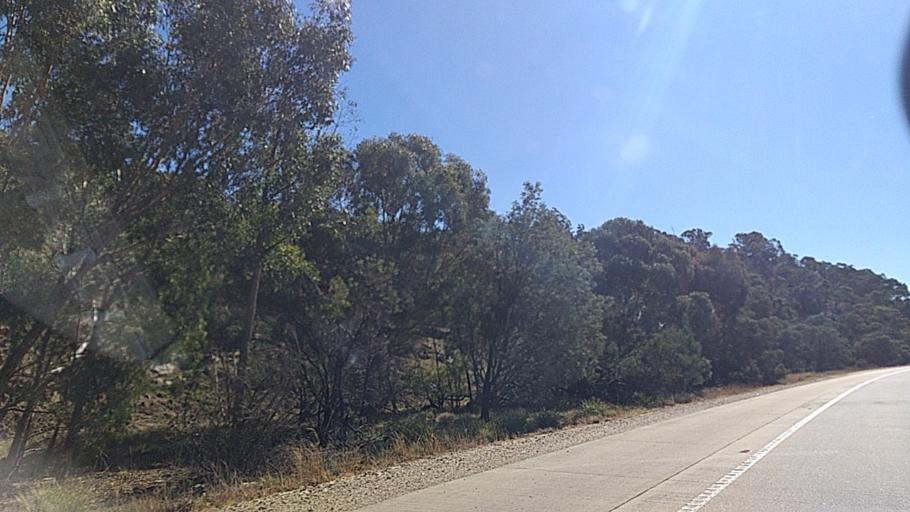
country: AU
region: New South Wales
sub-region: Yass Valley
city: Gundaroo
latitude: -35.0883
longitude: 149.3745
